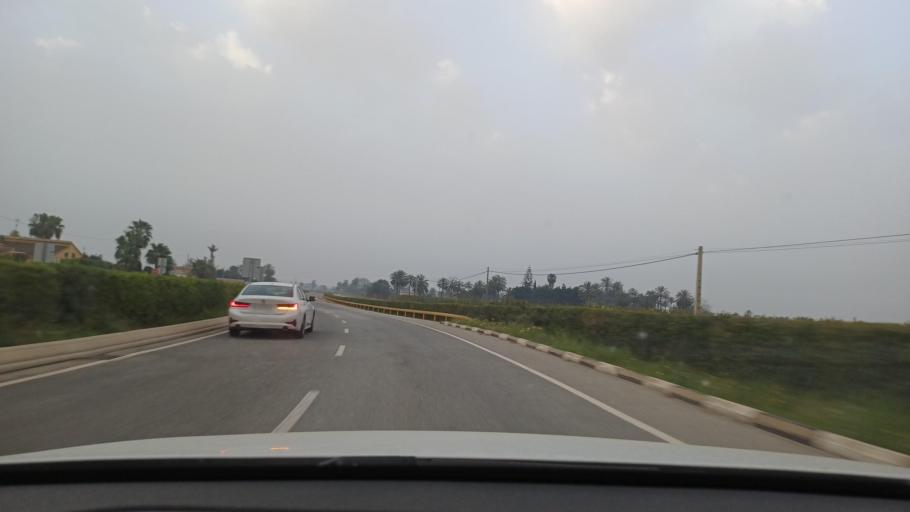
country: ES
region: Valencia
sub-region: Provincia de Alicante
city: Elche
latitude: 38.2138
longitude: -0.6976
